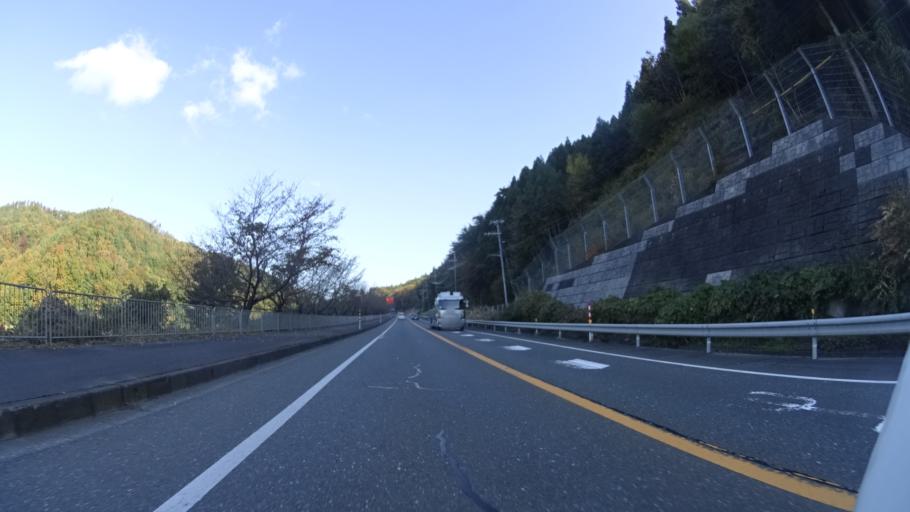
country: JP
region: Fukui
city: Tsuruga
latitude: 35.4746
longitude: 136.0812
